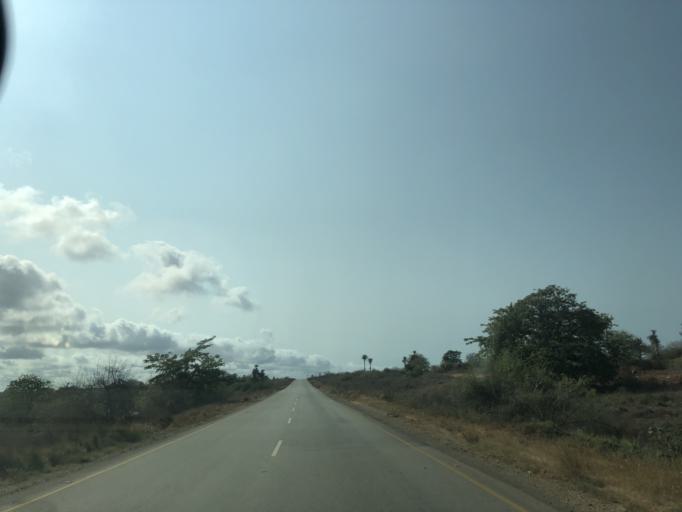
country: AO
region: Luanda
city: Luanda
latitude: -9.6995
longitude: 13.2119
